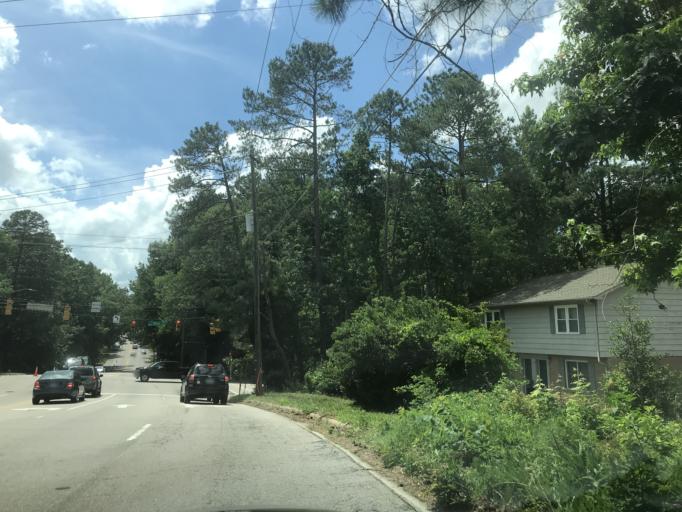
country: US
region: North Carolina
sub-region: Wake County
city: West Raleigh
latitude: 35.8011
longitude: -78.6755
